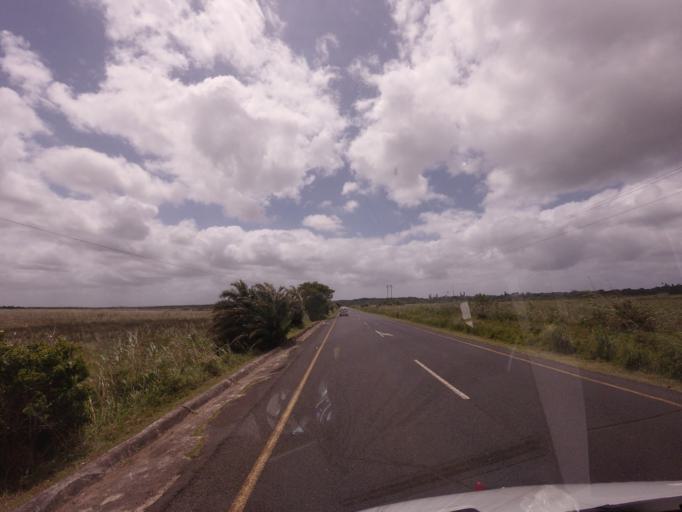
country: ZA
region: KwaZulu-Natal
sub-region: uMkhanyakude District Municipality
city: Mtubatuba
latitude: -28.3727
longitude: 32.3993
